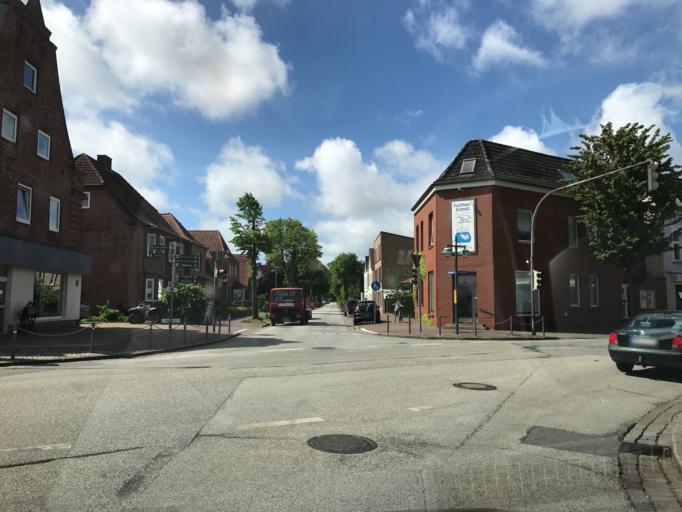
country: DE
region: Schleswig-Holstein
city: Brunsbuttel
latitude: 53.8970
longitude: 9.1372
